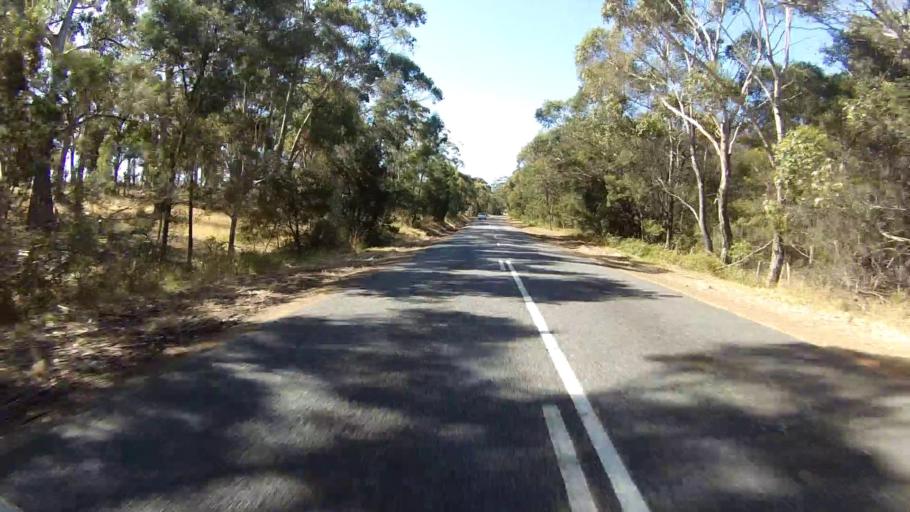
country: AU
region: Tasmania
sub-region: Sorell
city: Sorell
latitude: -42.3253
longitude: 147.9482
